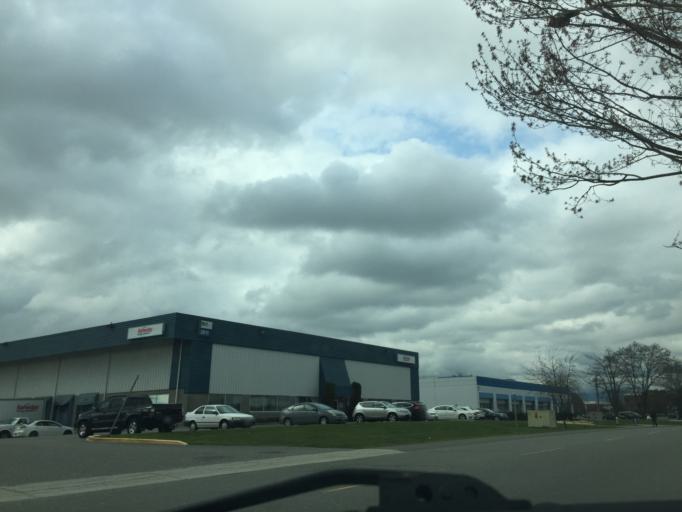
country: CA
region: British Columbia
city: Richmond
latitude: 49.1904
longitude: -123.1586
